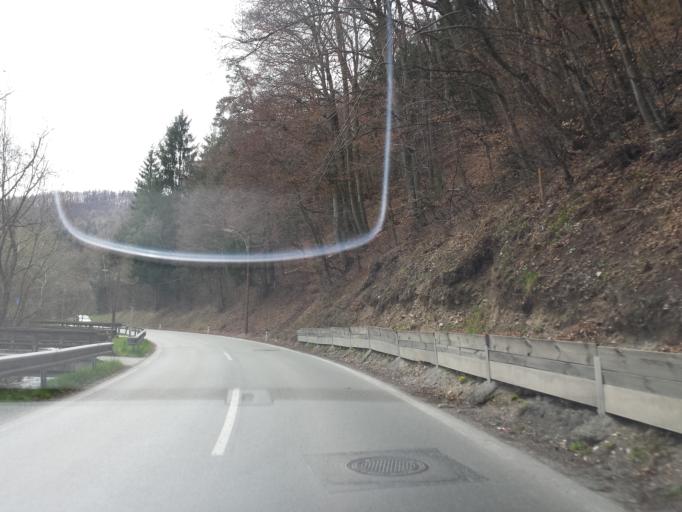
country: AT
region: Styria
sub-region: Graz Stadt
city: Goesting
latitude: 47.0995
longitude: 15.3780
